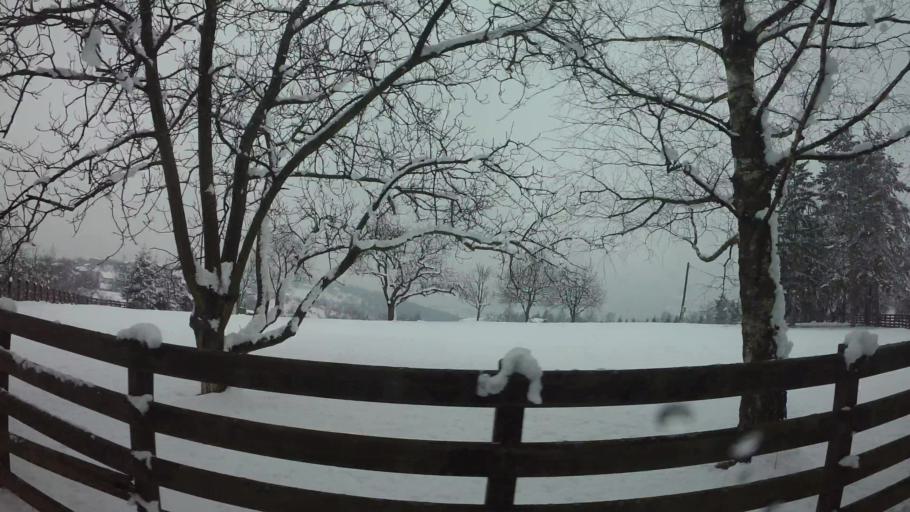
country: BA
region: Federation of Bosnia and Herzegovina
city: Hadzici
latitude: 43.8558
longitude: 18.2589
